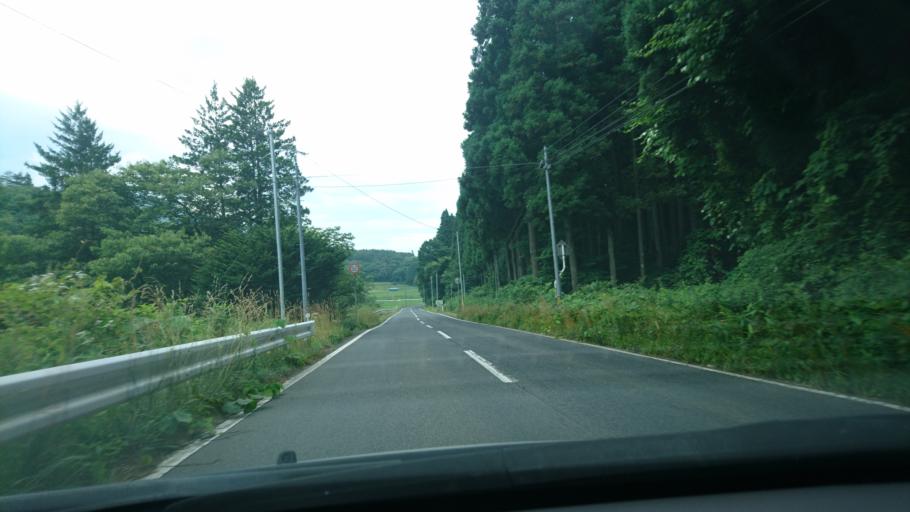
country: JP
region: Iwate
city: Ichinoseki
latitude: 38.8817
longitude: 141.4257
